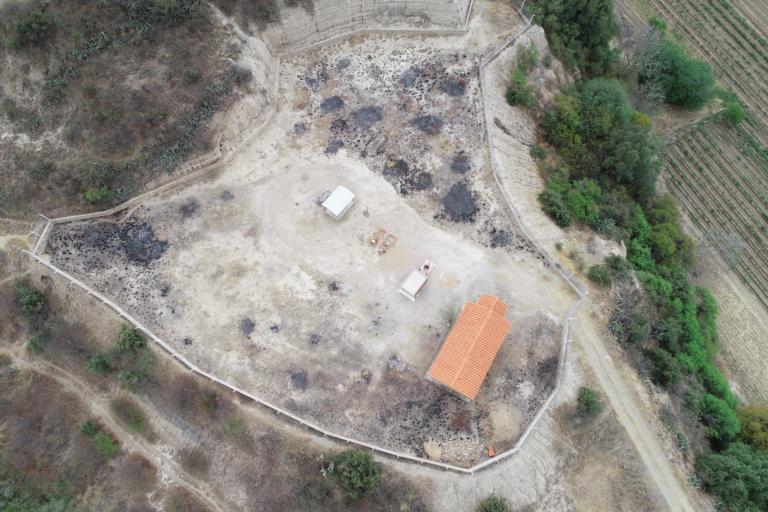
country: BO
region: Tarija
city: Tarija
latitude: -21.6008
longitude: -64.6190
